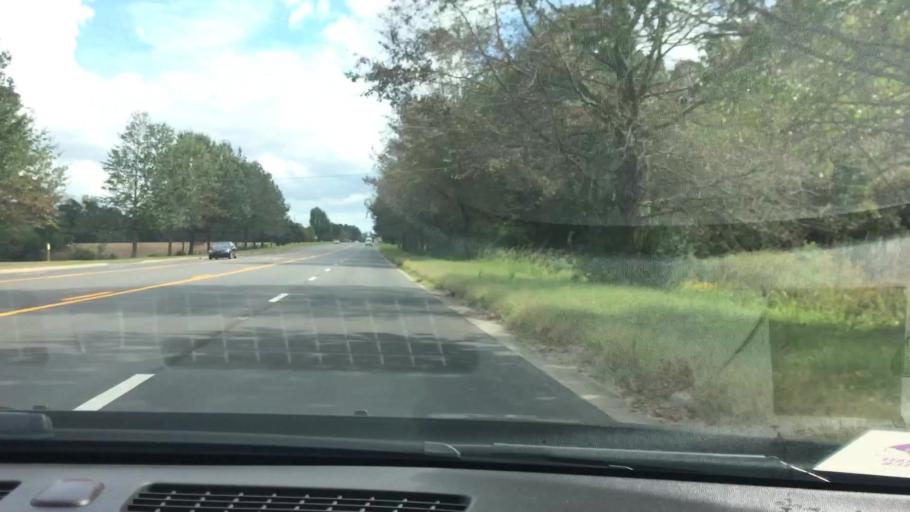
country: US
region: North Carolina
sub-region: Pitt County
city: Farmville
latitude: 35.5854
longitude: -77.6021
